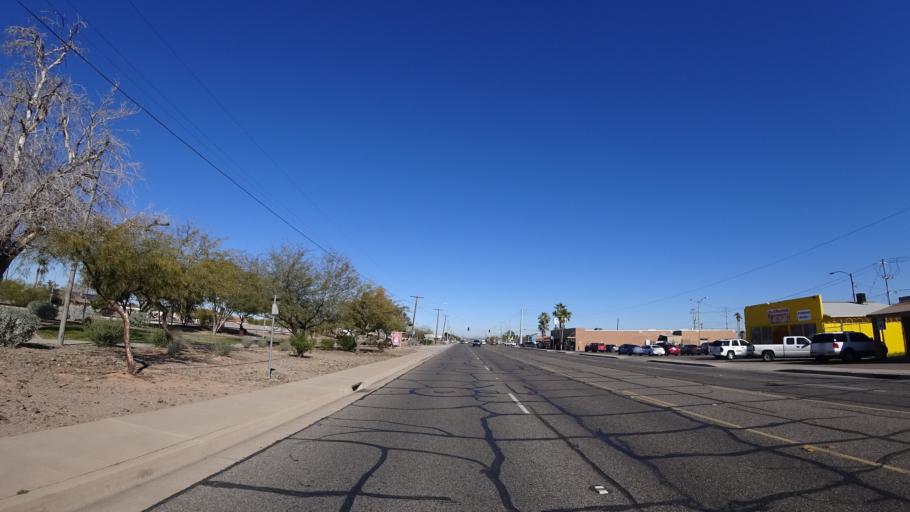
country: US
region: Arizona
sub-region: Maricopa County
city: Avondale
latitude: 33.4309
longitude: -112.3466
